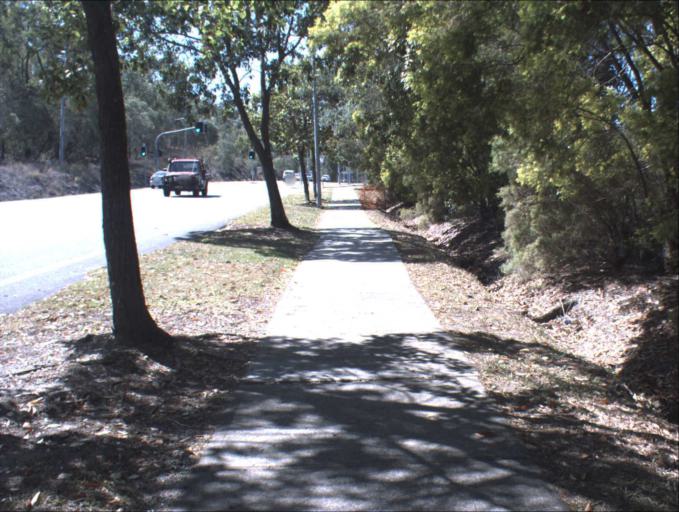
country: AU
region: Queensland
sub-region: Logan
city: Windaroo
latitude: -27.7325
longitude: 153.1927
